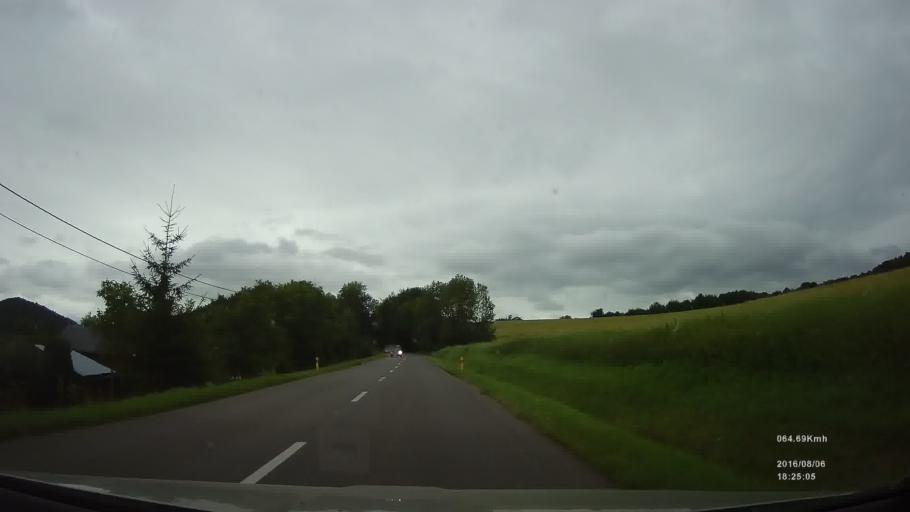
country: SK
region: Presovsky
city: Svidnik
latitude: 49.2936
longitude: 21.5730
